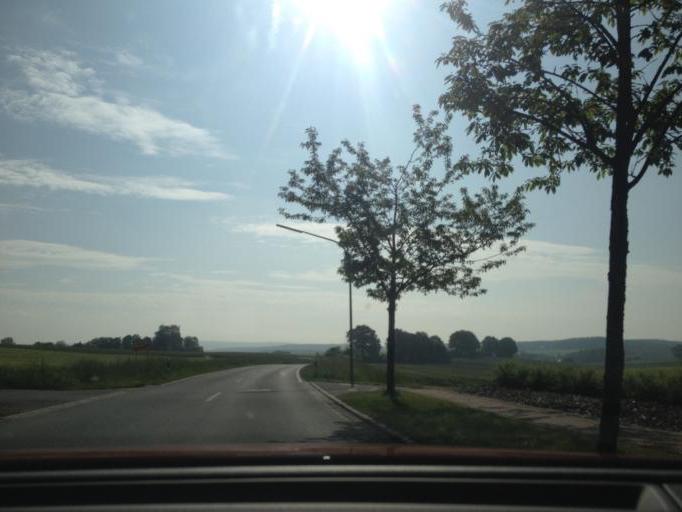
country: DE
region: Bavaria
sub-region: Upper Palatinate
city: Trabitz
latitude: 49.8012
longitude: 11.8733
